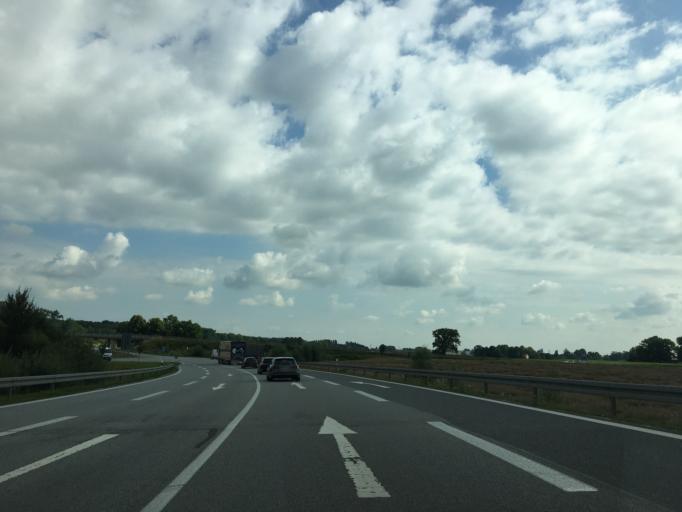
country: DE
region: Bavaria
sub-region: Upper Bavaria
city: Poing
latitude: 48.1610
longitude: 11.8332
